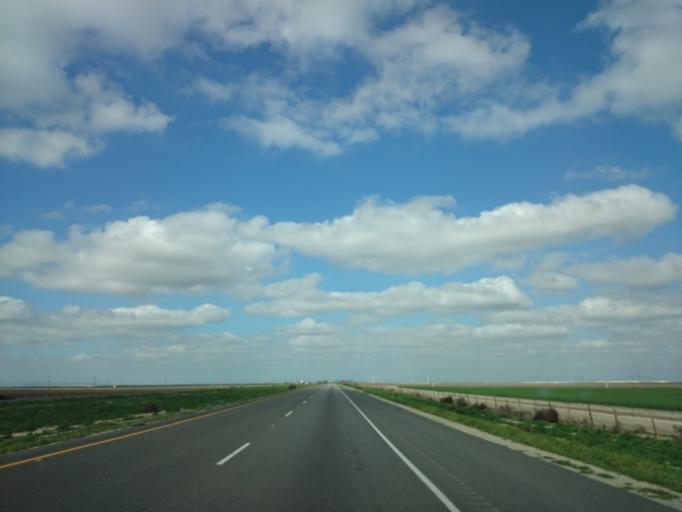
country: US
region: California
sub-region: Kern County
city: Greenfield
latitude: 35.1887
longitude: -119.1405
